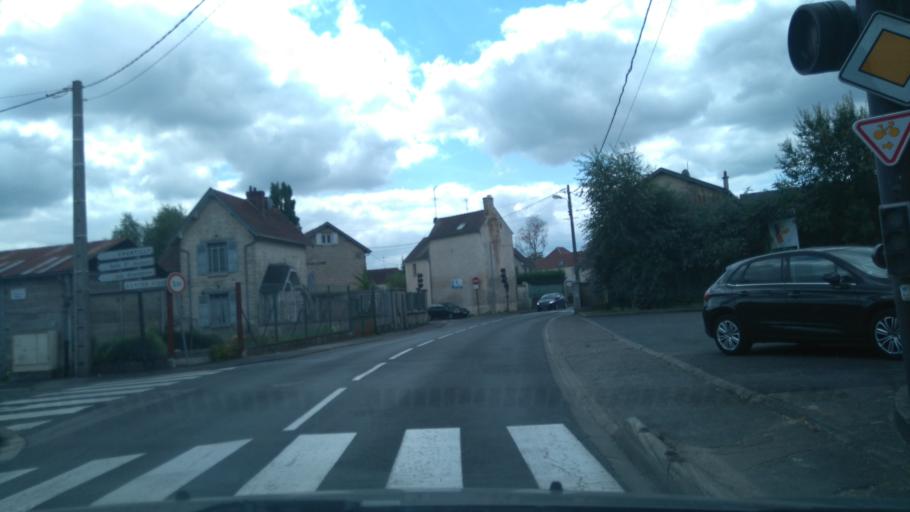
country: FR
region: Picardie
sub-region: Departement de l'Oise
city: Gouvieux
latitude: 49.1920
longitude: 2.4179
